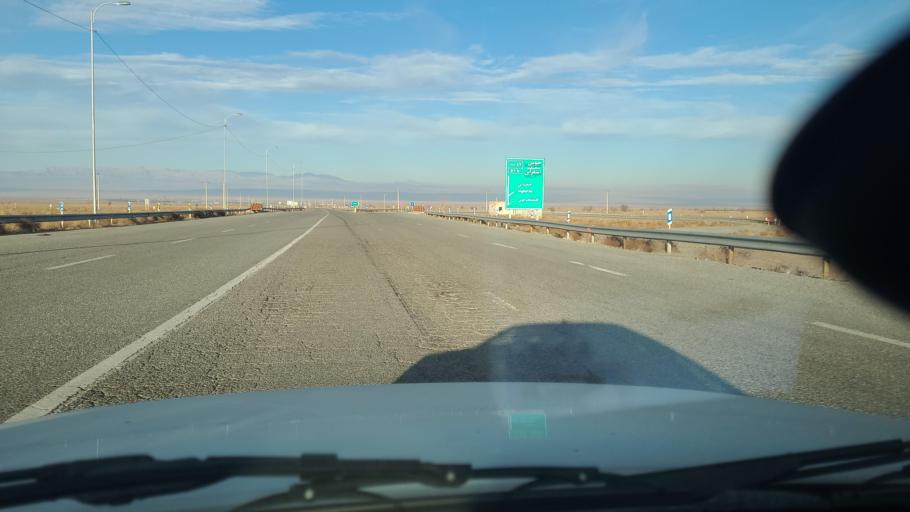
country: IR
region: Razavi Khorasan
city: Neqab
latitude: 36.5124
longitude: 57.5397
